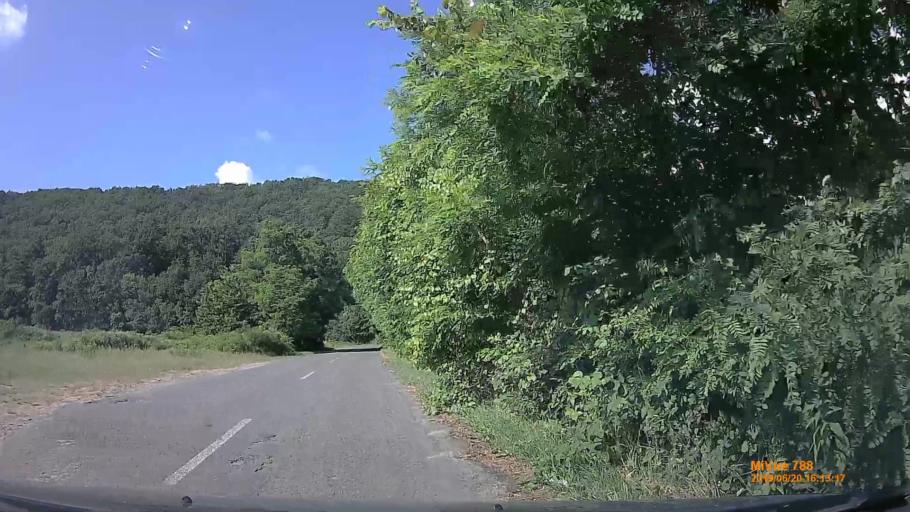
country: HU
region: Baranya
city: Pellerd
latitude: 46.0997
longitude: 18.0908
